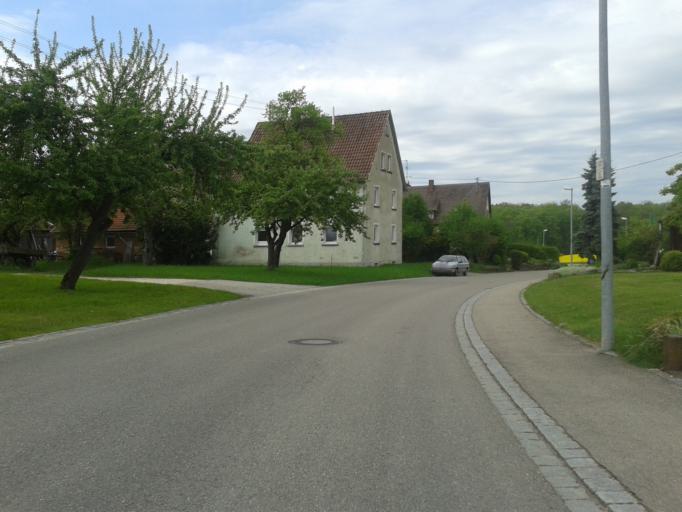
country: DE
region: Baden-Wuerttemberg
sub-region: Tuebingen Region
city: Erbach
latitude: 48.3696
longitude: 9.8393
